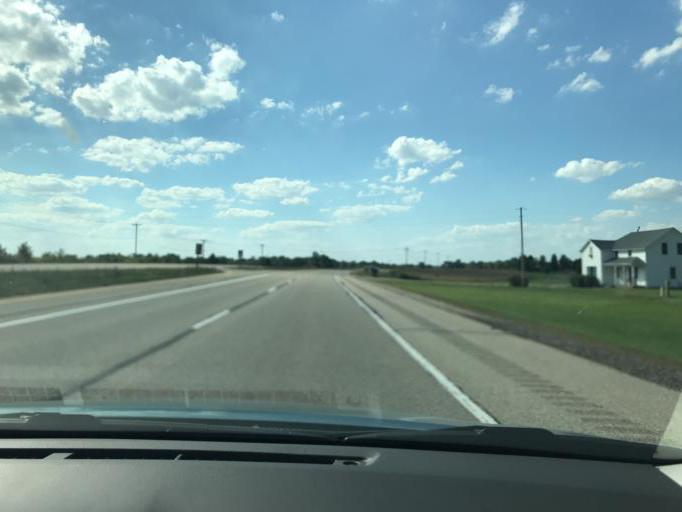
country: US
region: Wisconsin
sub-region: Kenosha County
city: Powers Lake
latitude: 42.5816
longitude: -88.3253
